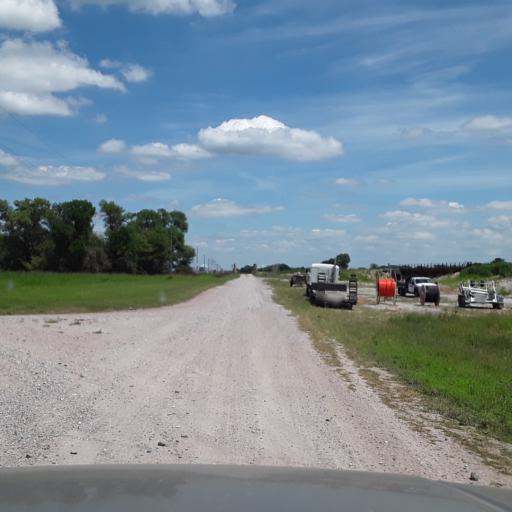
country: US
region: Nebraska
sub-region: Polk County
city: Osceola
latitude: 41.3525
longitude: -97.5797
